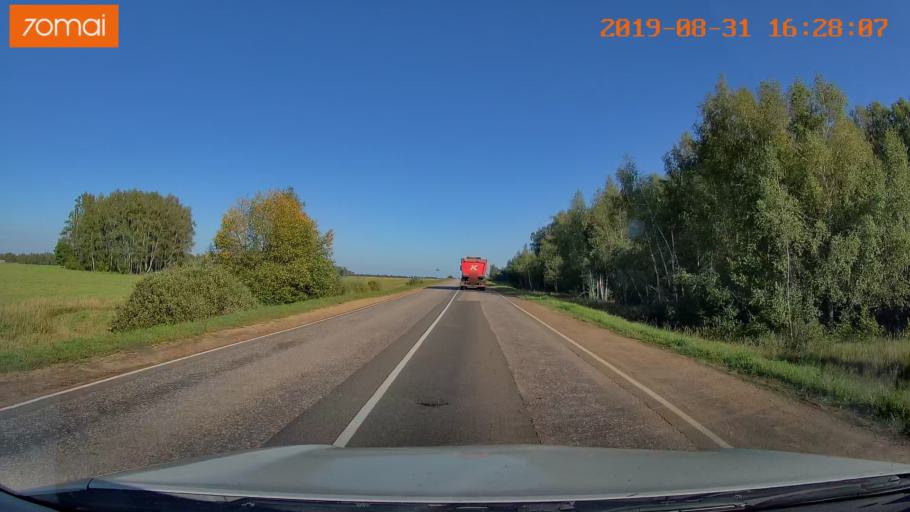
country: RU
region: Kaluga
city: Babynino
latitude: 54.5111
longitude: 35.7726
